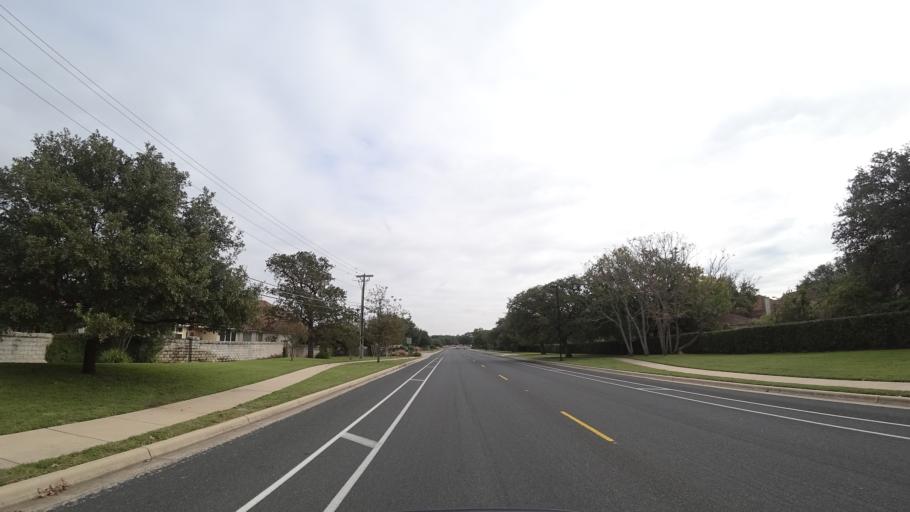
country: US
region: Texas
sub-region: Travis County
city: Shady Hollow
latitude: 30.1949
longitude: -97.8910
